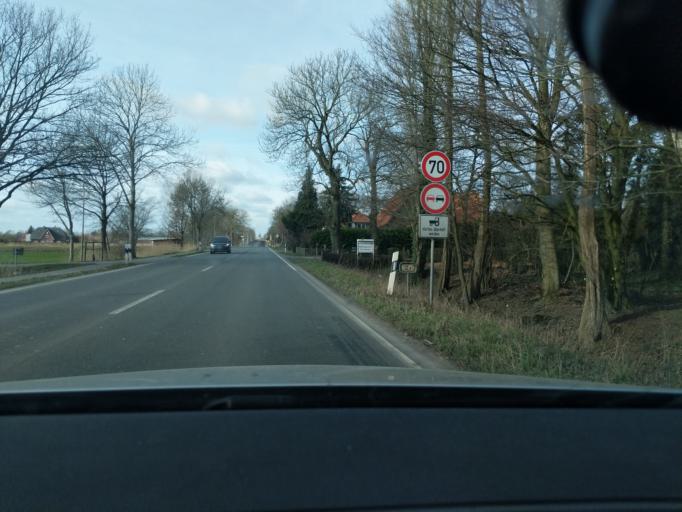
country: DE
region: Lower Saxony
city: Drochtersen
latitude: 53.7036
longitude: 9.4029
